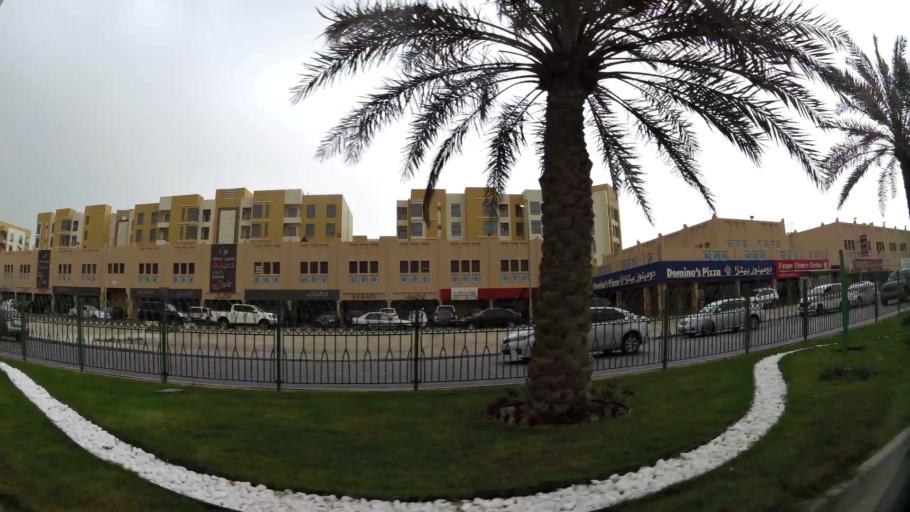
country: BH
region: Northern
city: Madinat `Isa
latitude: 26.1694
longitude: 50.5513
